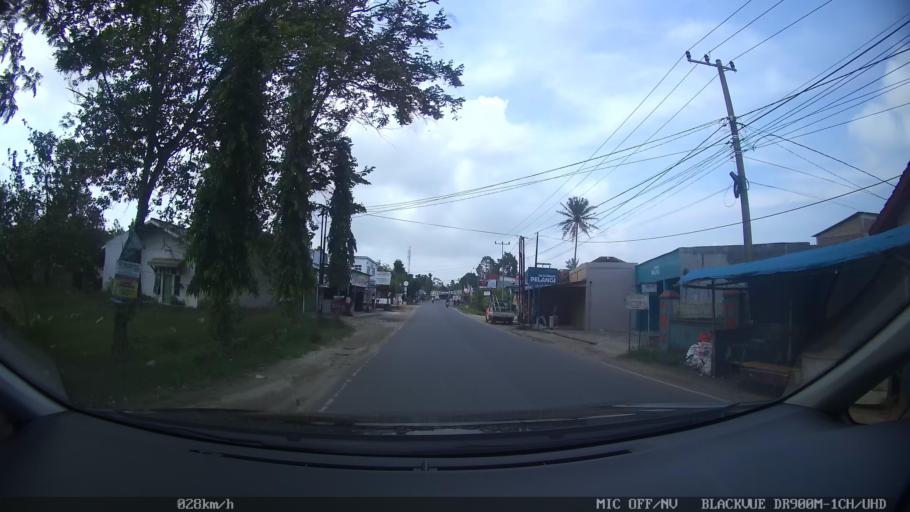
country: ID
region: Lampung
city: Kedaton
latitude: -5.3216
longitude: 105.2894
